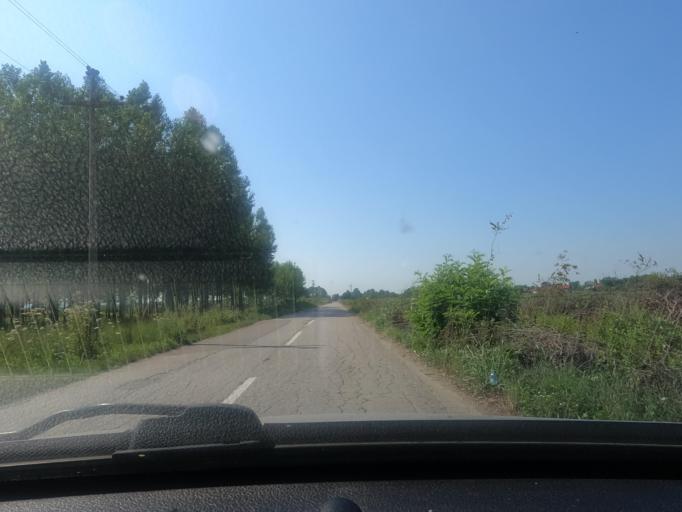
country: RS
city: Lipnicki Sor
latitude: 44.5741
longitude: 19.2782
